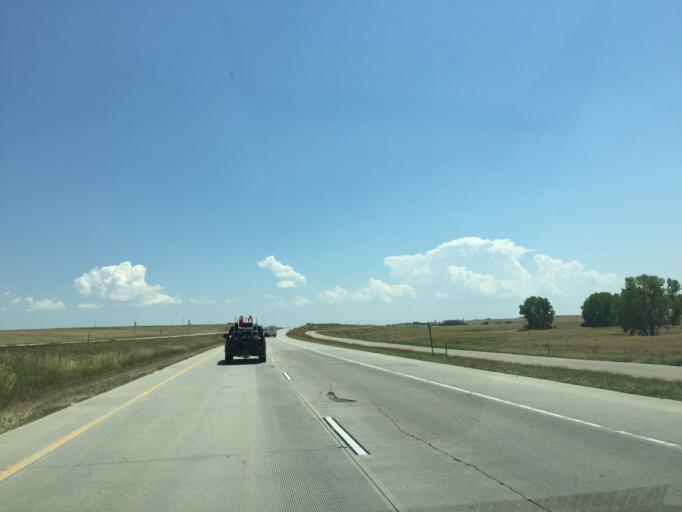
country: US
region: Colorado
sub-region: Arapahoe County
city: Byers
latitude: 39.4929
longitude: -103.9607
